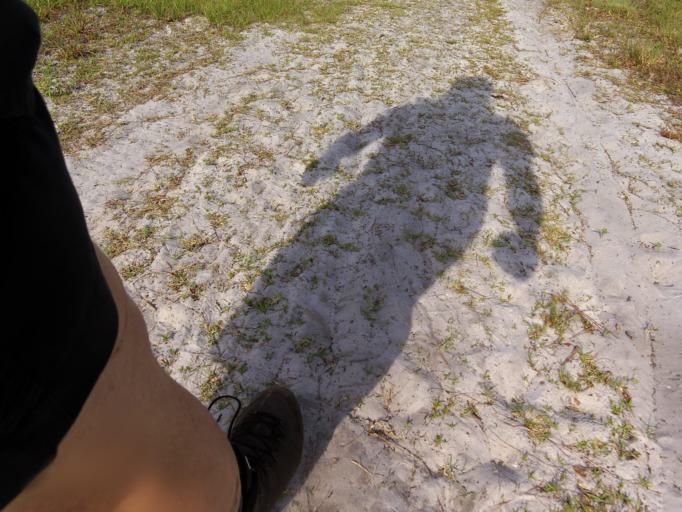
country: US
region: Florida
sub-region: Saint Johns County
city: Villano Beach
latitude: 30.0278
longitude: -81.3409
